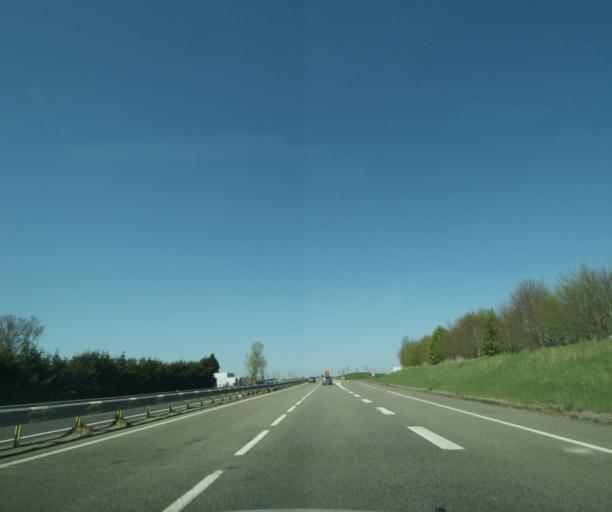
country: FR
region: Bourgogne
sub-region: Departement de la Nievre
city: Cosne-Cours-sur-Loire
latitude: 47.3800
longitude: 2.9232
